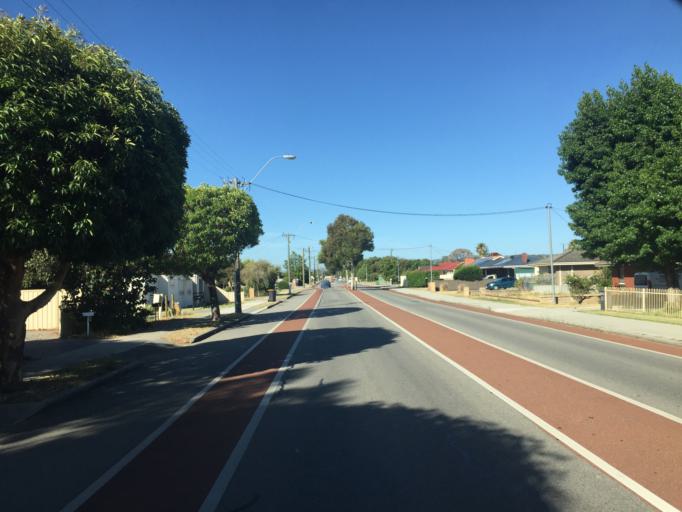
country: AU
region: Western Australia
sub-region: Canning
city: East Cannington
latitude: -32.0123
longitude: 115.9668
